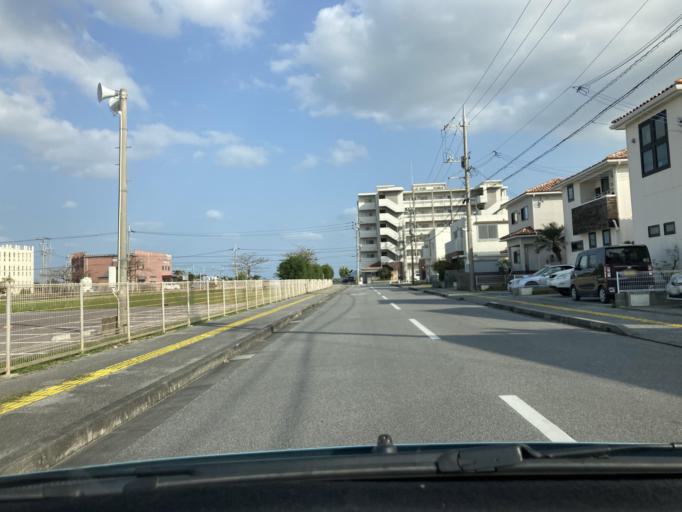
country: JP
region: Okinawa
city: Ginowan
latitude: 26.2093
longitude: 127.7624
